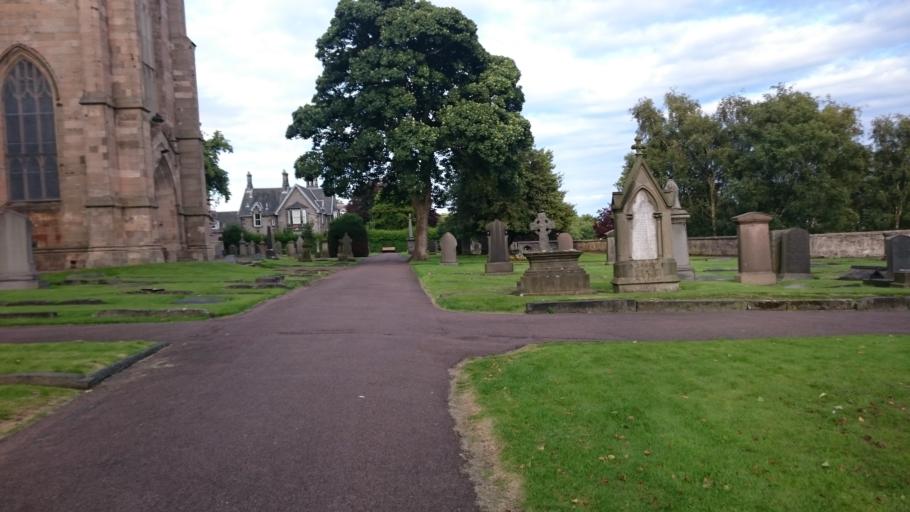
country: GB
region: Scotland
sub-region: Fife
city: Dunfermline
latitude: 56.0697
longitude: -3.4637
